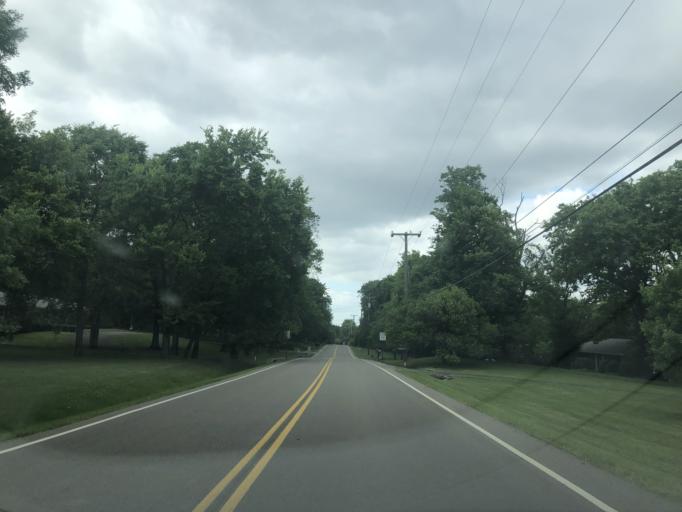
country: US
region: Tennessee
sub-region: Davidson County
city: Forest Hills
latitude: 36.0878
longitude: -86.8201
